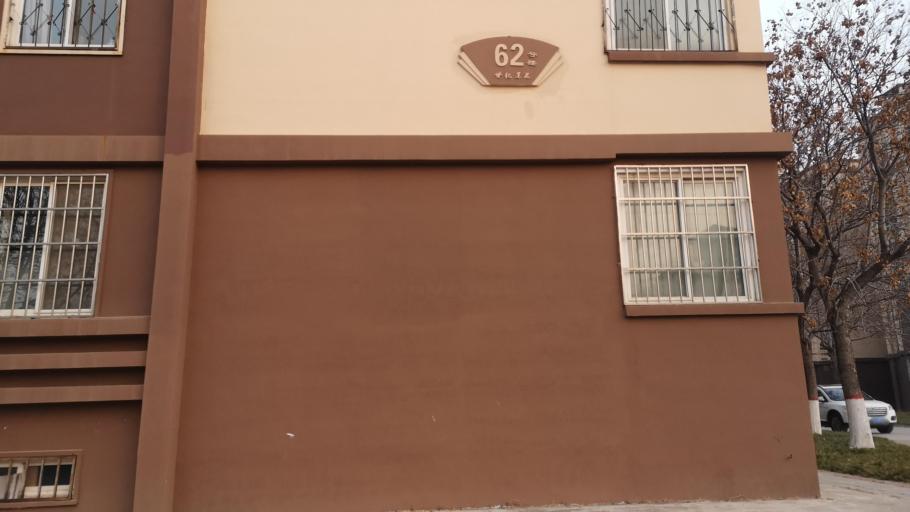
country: CN
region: Henan Sheng
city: Zhongyuanlu
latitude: 35.7881
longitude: 115.0752
